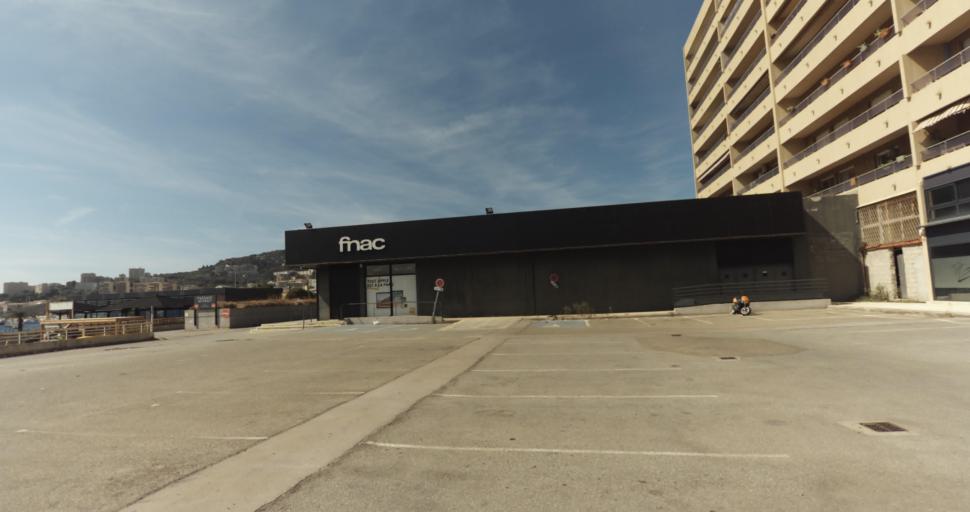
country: FR
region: Corsica
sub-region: Departement de la Corse-du-Sud
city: Ajaccio
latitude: 41.9328
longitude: 8.7481
